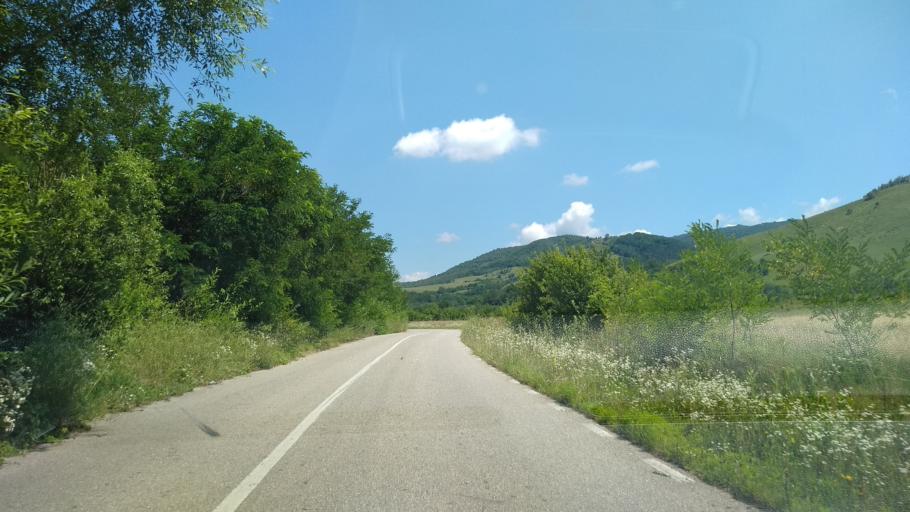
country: RO
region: Hunedoara
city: Berca
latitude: 45.6283
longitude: 23.0265
